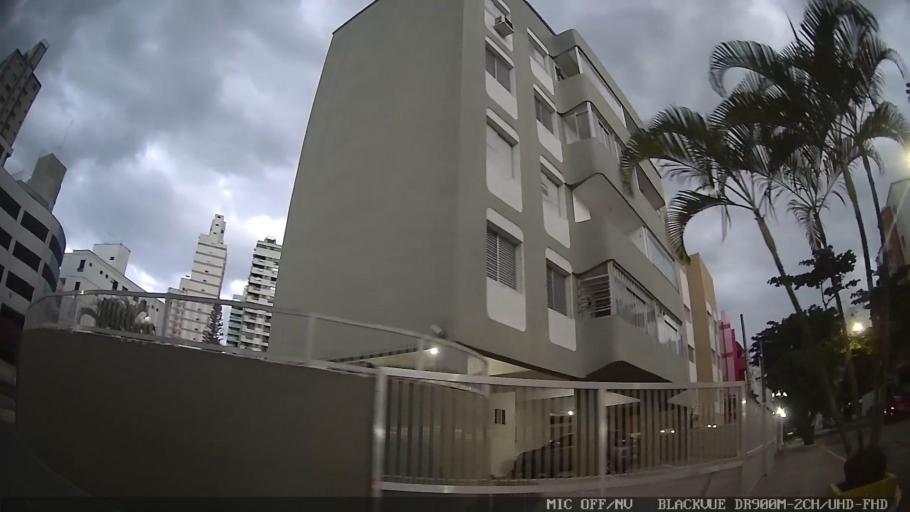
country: BR
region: Sao Paulo
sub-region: Guaruja
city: Guaruja
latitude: -24.0081
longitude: -46.2719
